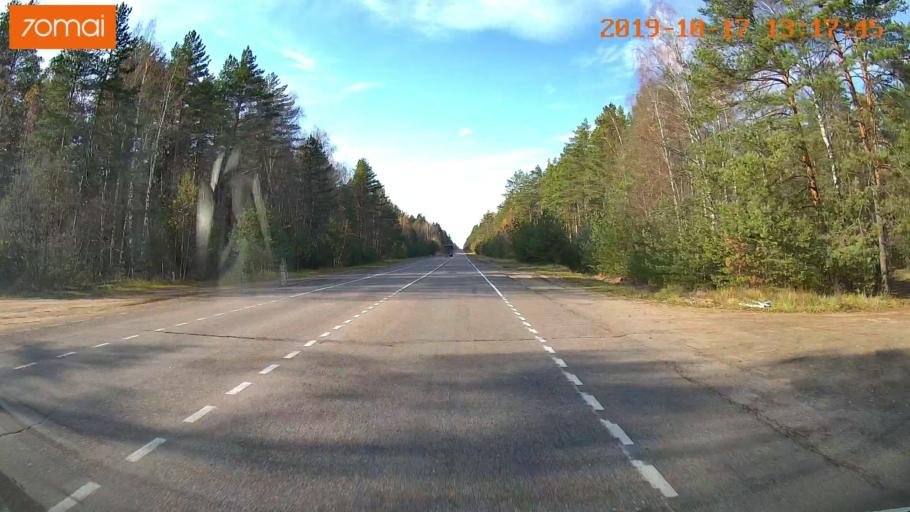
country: RU
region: Rjazan
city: Gus'-Zheleznyy
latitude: 55.0586
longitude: 41.1141
